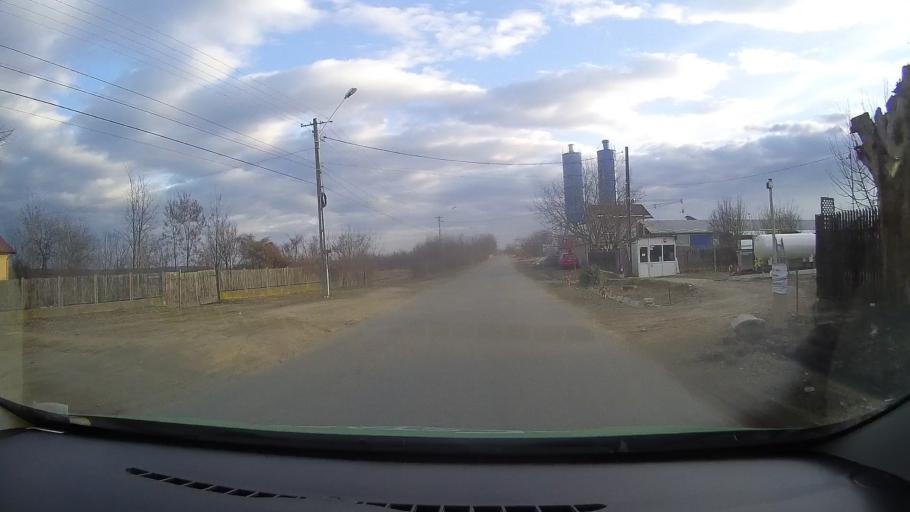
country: RO
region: Dambovita
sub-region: Municipiul Moreni
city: Moreni
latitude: 44.9607
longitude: 25.6572
